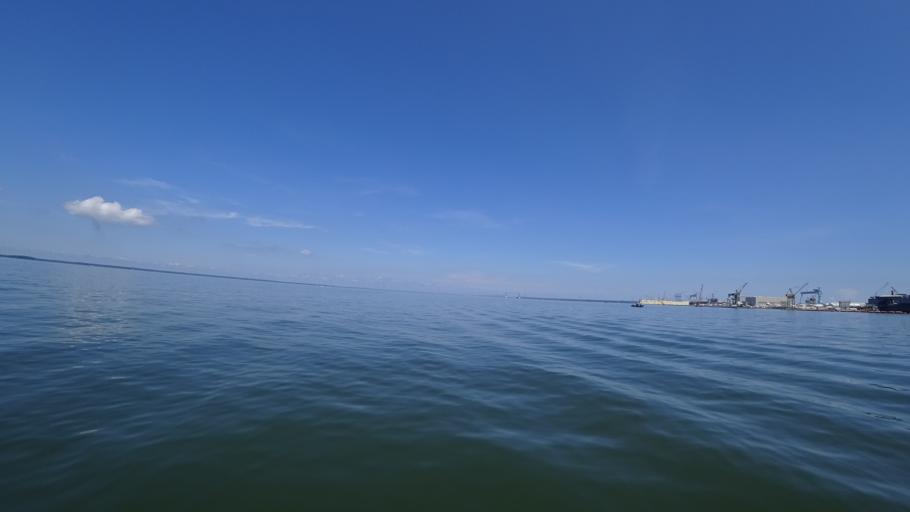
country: US
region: Virginia
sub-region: City of Newport News
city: Newport News
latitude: 36.9756
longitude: -76.4423
